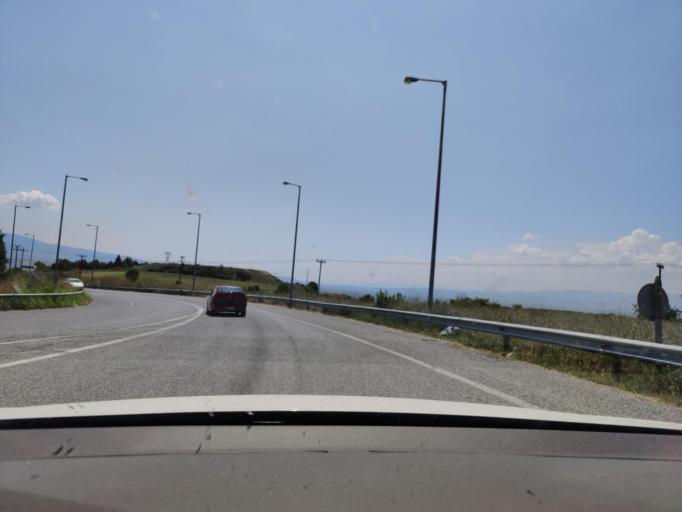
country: GR
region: Central Macedonia
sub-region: Nomos Serron
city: Nea Zichni
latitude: 41.0158
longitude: 23.8491
